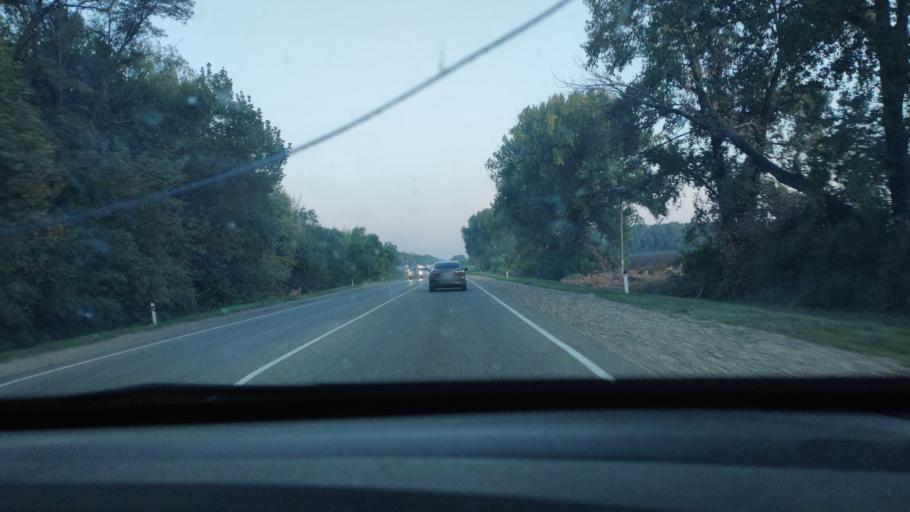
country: RU
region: Krasnodarskiy
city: Medvedovskaya
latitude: 45.4591
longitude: 38.9865
